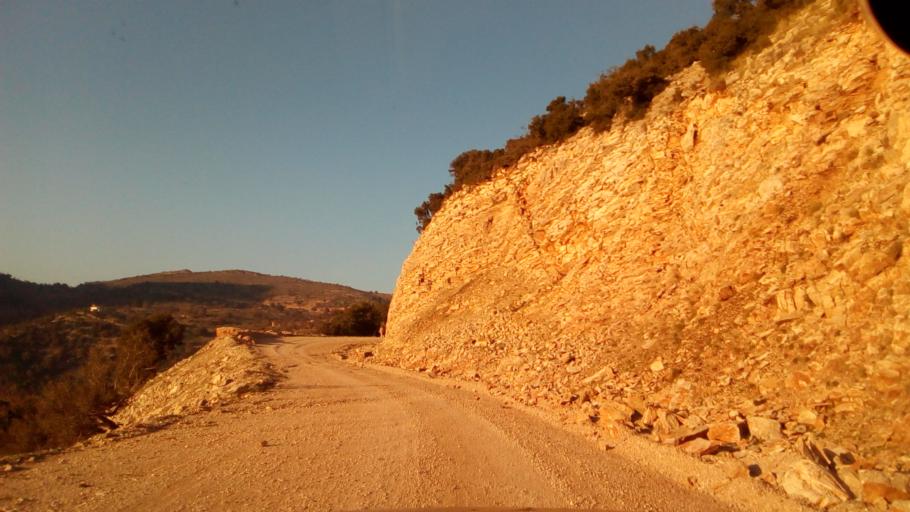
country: GR
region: West Greece
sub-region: Nomos Aitolias kai Akarnanias
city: Nafpaktos
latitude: 38.4479
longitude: 21.8436
